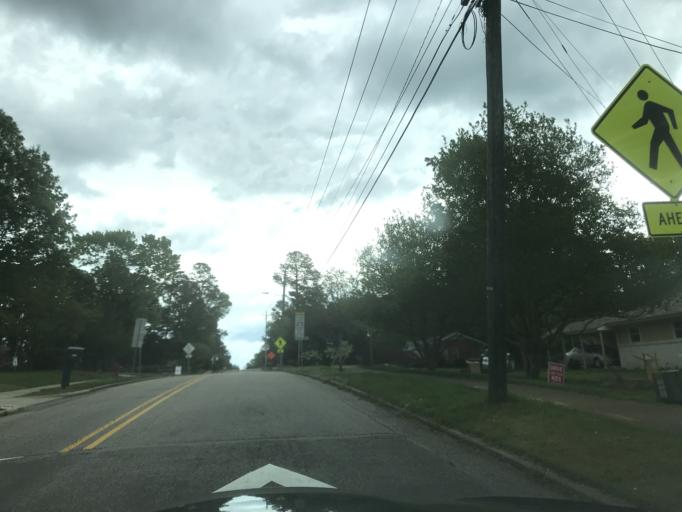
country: US
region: North Carolina
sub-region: Wake County
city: West Raleigh
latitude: 35.7773
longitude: -78.7053
